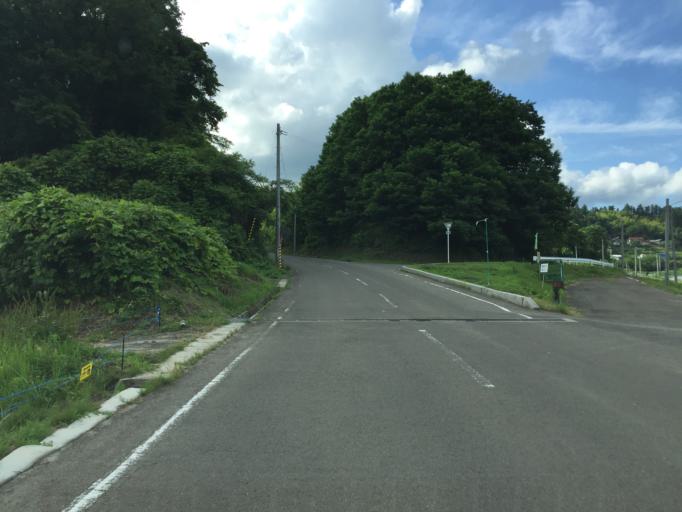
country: JP
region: Fukushima
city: Fukushima-shi
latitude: 37.6676
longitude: 140.5470
